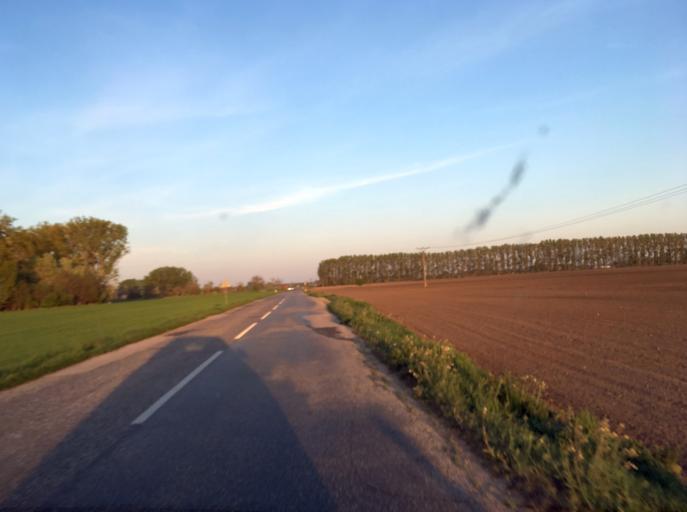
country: SK
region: Nitriansky
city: Kolarovo
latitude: 47.9036
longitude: 17.8774
